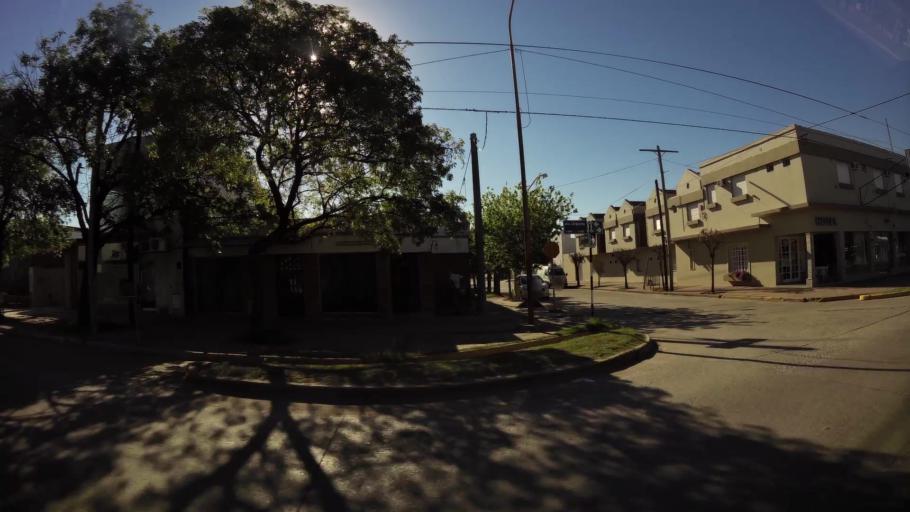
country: AR
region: Cordoba
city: San Francisco
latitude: -31.4177
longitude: -62.0948
